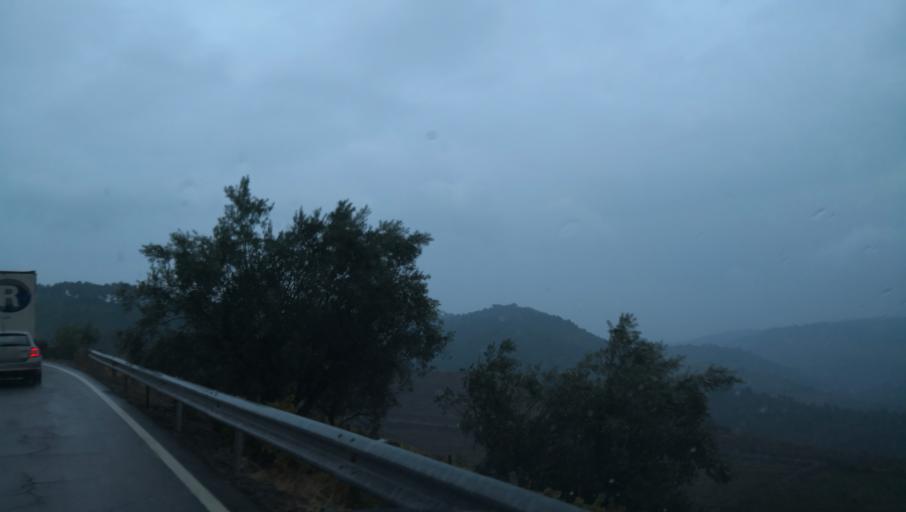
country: PT
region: Vila Real
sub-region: Vila Real
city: Vila Real
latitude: 41.2345
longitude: -7.7271
